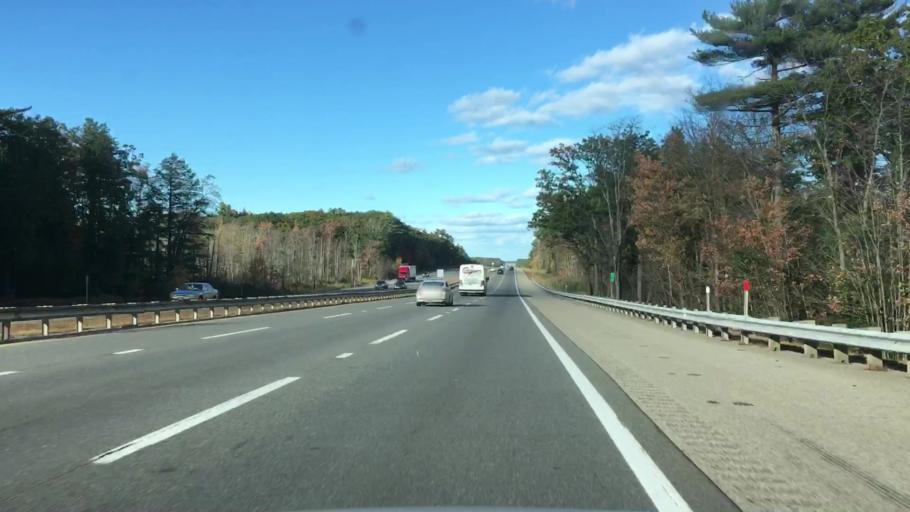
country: US
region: Maine
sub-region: York County
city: Wells Beach Station
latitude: 43.3604
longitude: -70.5873
